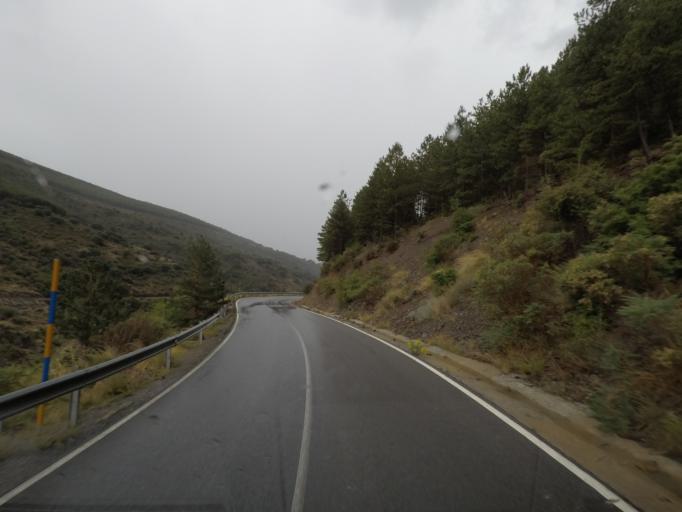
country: ES
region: Andalusia
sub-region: Provincia de Almeria
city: Bayarcal
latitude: 37.0714
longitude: -3.0183
